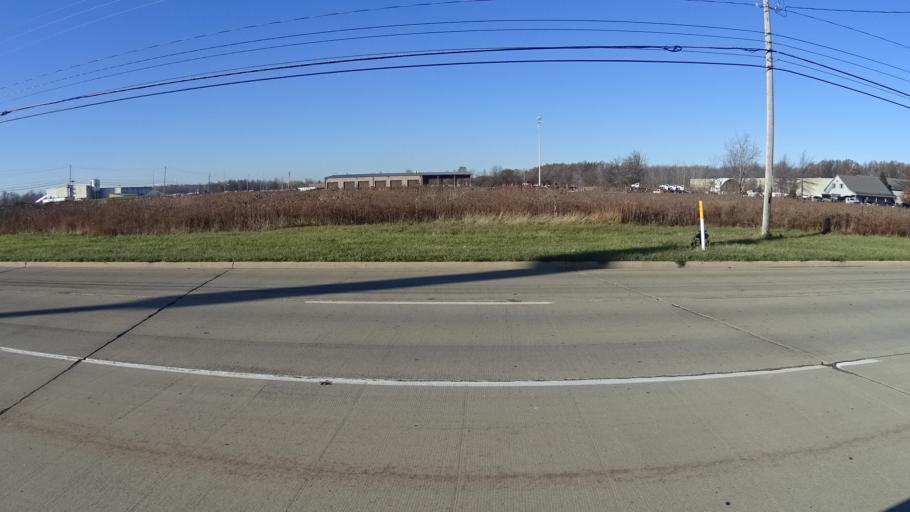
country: US
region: Ohio
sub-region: Lorain County
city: Sheffield Lake
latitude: 41.4831
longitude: -82.0757
